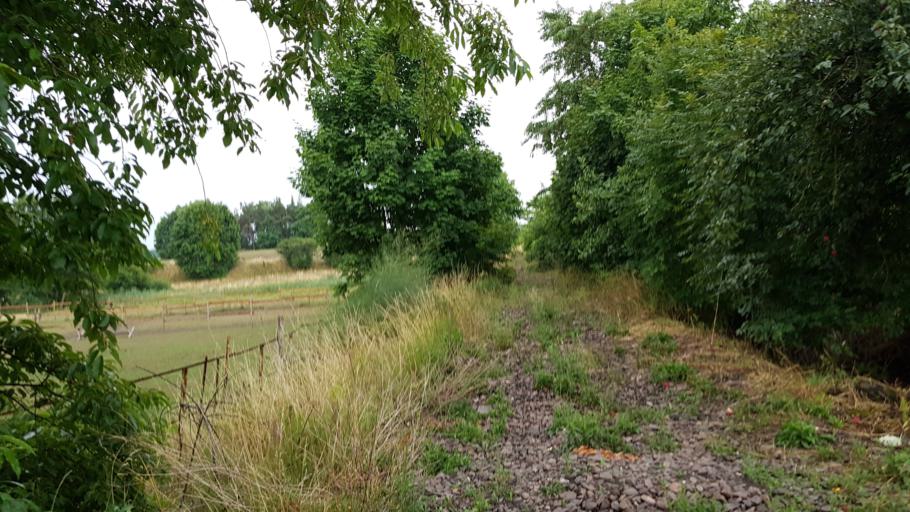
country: PL
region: West Pomeranian Voivodeship
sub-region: Powiat walecki
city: Walcz
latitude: 53.3173
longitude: 16.4416
